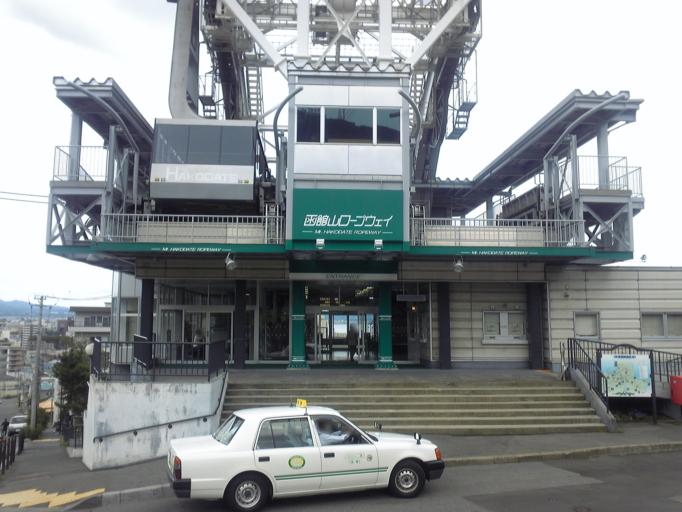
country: JP
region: Hokkaido
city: Hakodate
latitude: 41.7608
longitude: 140.7140
